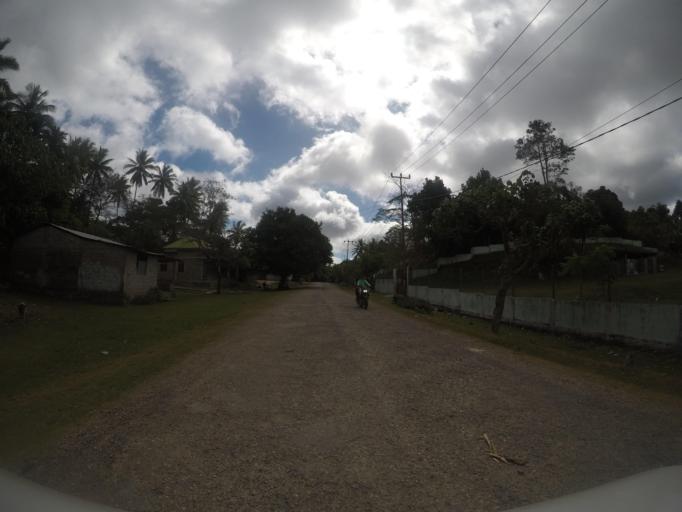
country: TL
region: Lautem
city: Lospalos
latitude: -8.5431
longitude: 126.9451
